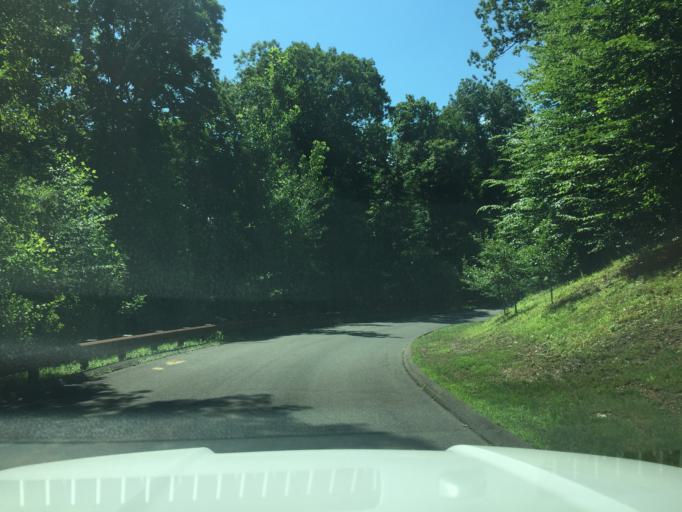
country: US
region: Connecticut
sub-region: Fairfield County
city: Westport
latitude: 41.2166
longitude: -73.3539
